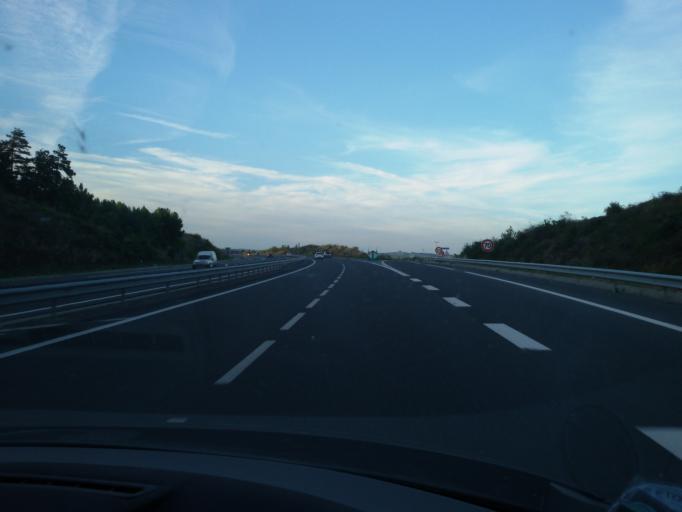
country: FR
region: Midi-Pyrenees
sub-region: Departement de l'Aveyron
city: Millau
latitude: 44.1661
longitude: 3.0297
